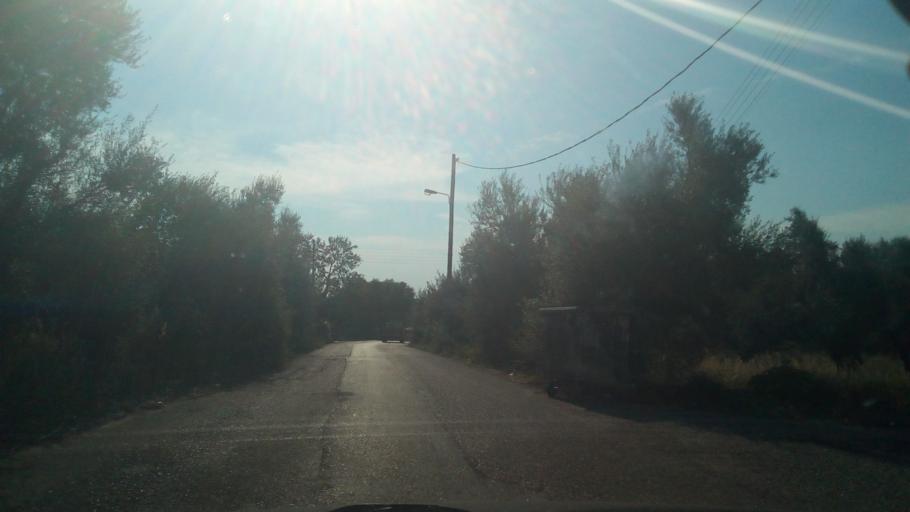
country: GR
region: West Greece
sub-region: Nomos Aitolias kai Akarnanias
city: Nafpaktos
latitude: 38.4036
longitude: 21.8547
